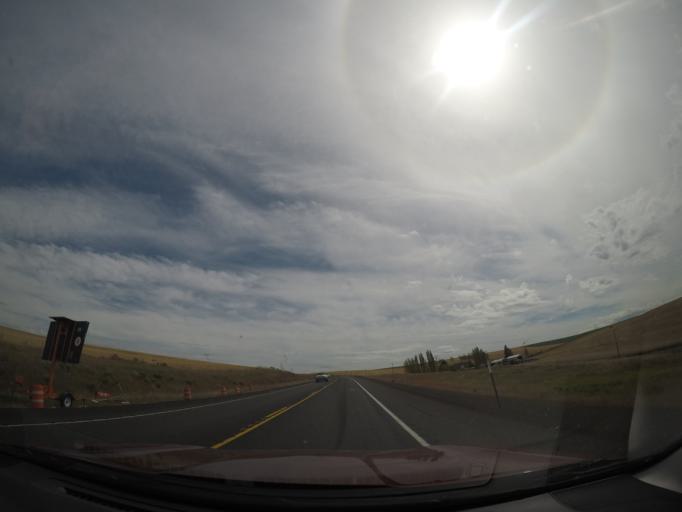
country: US
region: Oregon
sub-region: Sherman County
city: Moro
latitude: 45.5651
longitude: -120.6937
